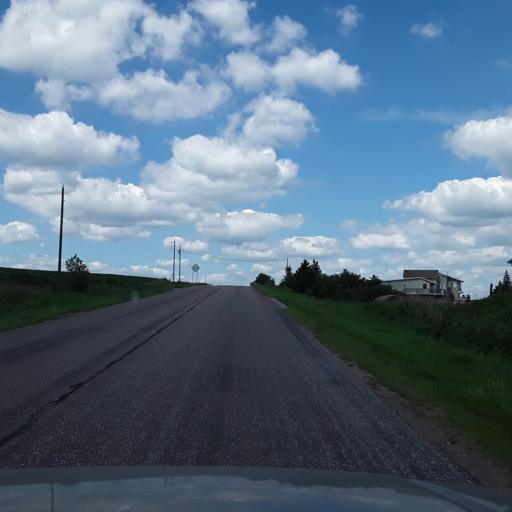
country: US
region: Nebraska
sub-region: Nance County
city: Genoa
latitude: 41.4745
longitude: -97.6958
